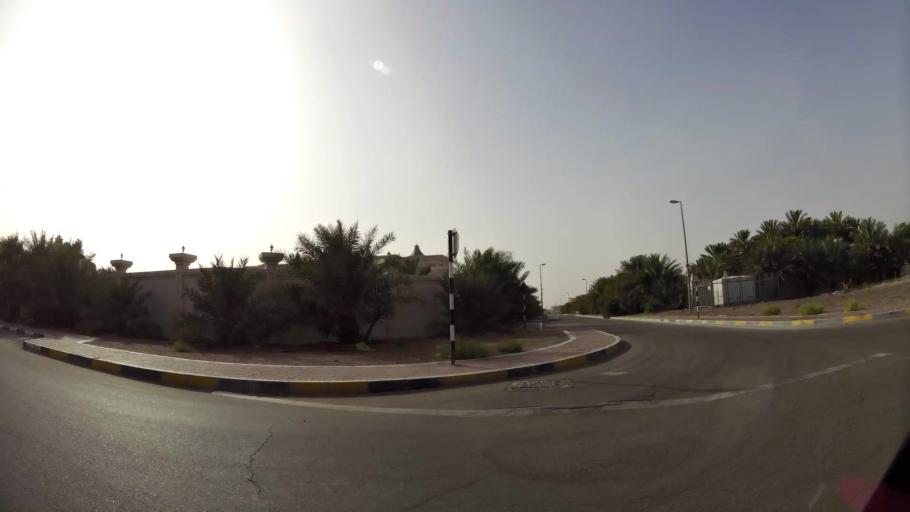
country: AE
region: Abu Dhabi
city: Al Ain
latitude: 24.2181
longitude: 55.6535
